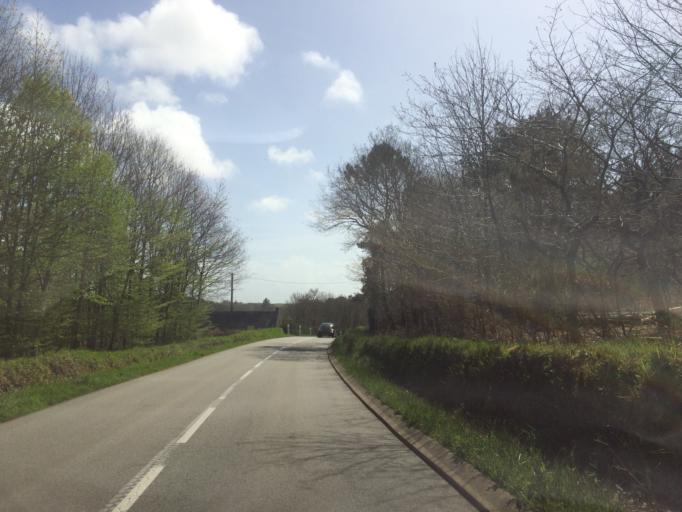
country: FR
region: Brittany
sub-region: Departement du Morbihan
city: Ploemel
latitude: 47.6340
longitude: -3.0477
